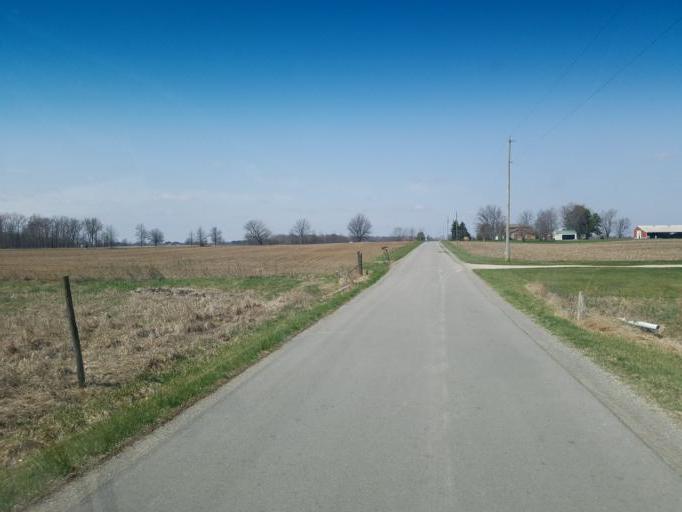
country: US
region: Ohio
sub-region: Wyandot County
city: Upper Sandusky
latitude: 40.8762
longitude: -83.3373
